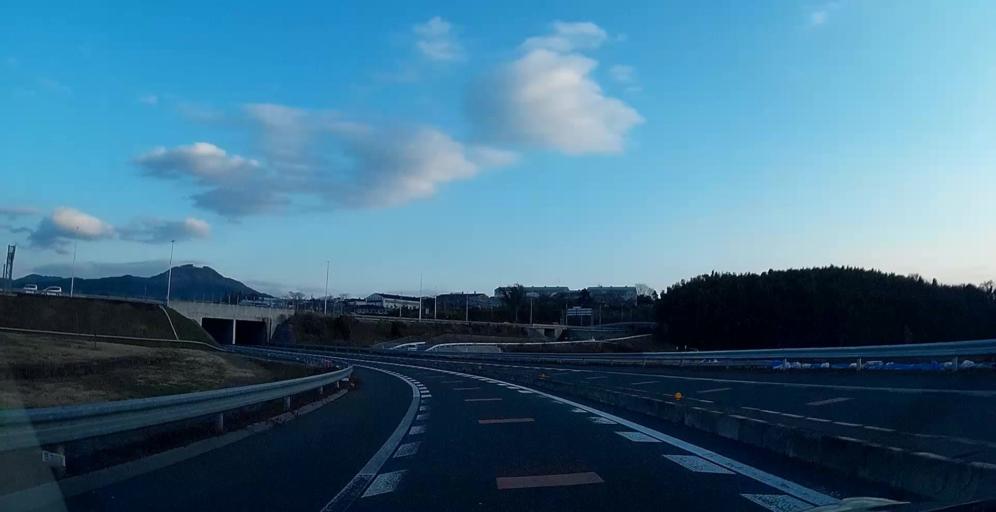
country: JP
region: Kumamoto
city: Kumamoto
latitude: 32.7545
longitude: 130.7875
